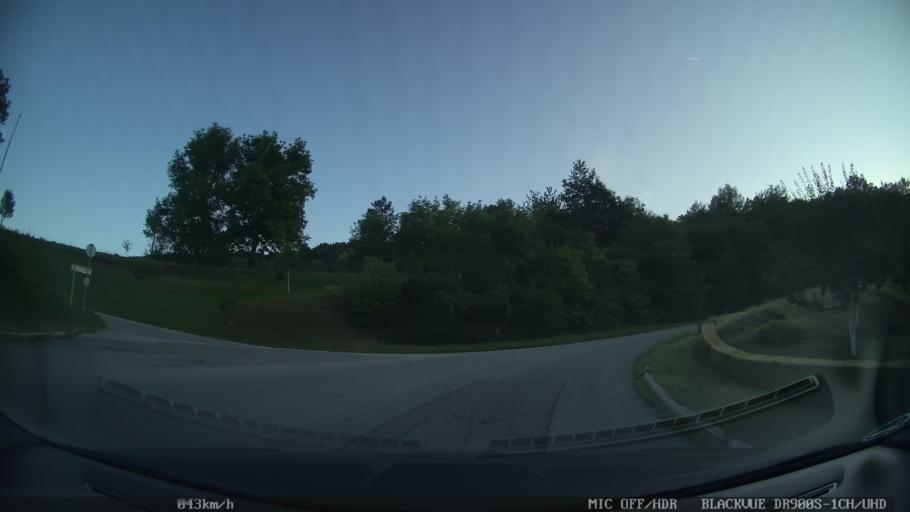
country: HR
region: Karlovacka
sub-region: Grad Ogulin
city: Ogulin
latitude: 45.2673
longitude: 15.1917
